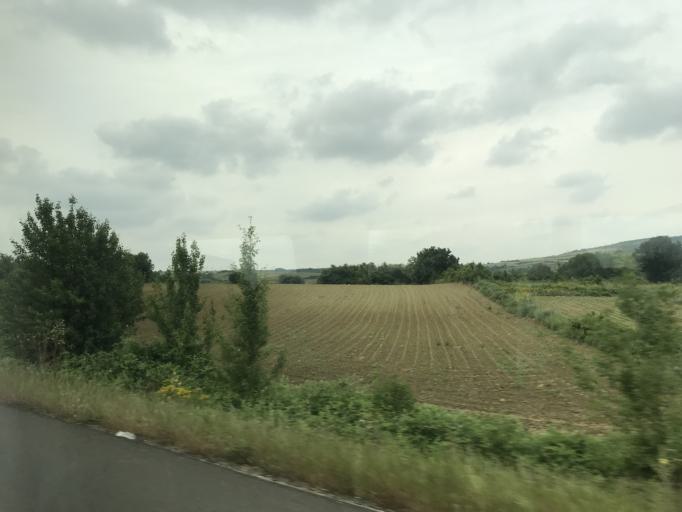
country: TR
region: Tekirdag
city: Malkara
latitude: 40.8663
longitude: 26.8419
